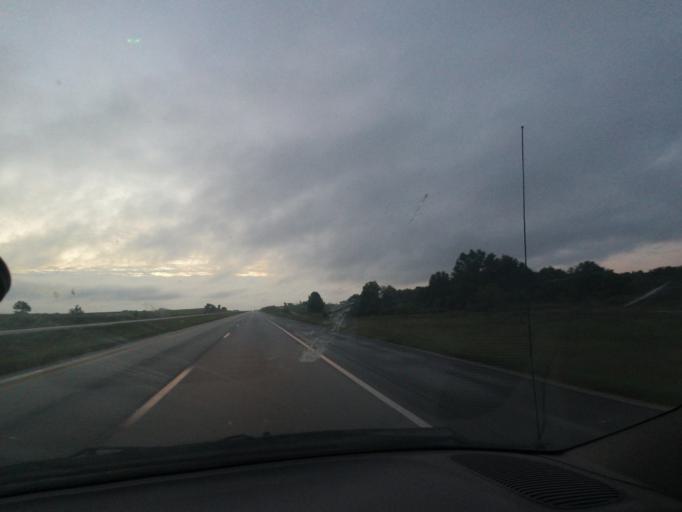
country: US
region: Missouri
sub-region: Linn County
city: Brookfield
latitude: 39.7629
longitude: -93.0229
